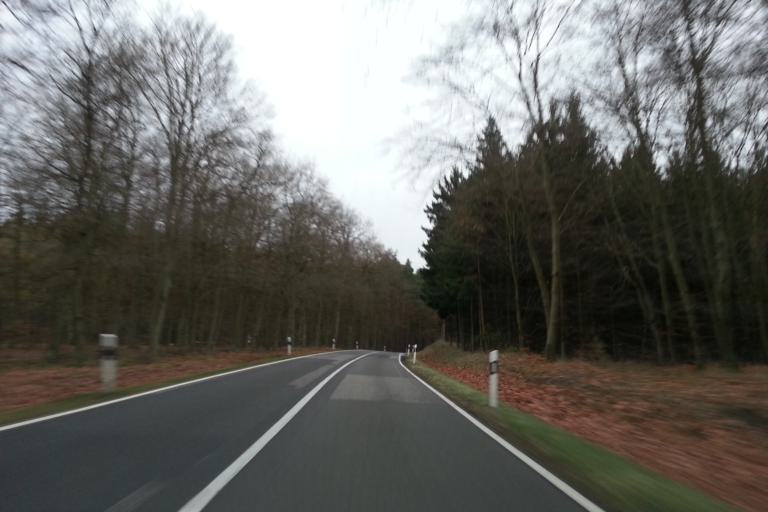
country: DE
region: Mecklenburg-Vorpommern
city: Ferdinandshof
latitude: 53.5988
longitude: 13.8585
